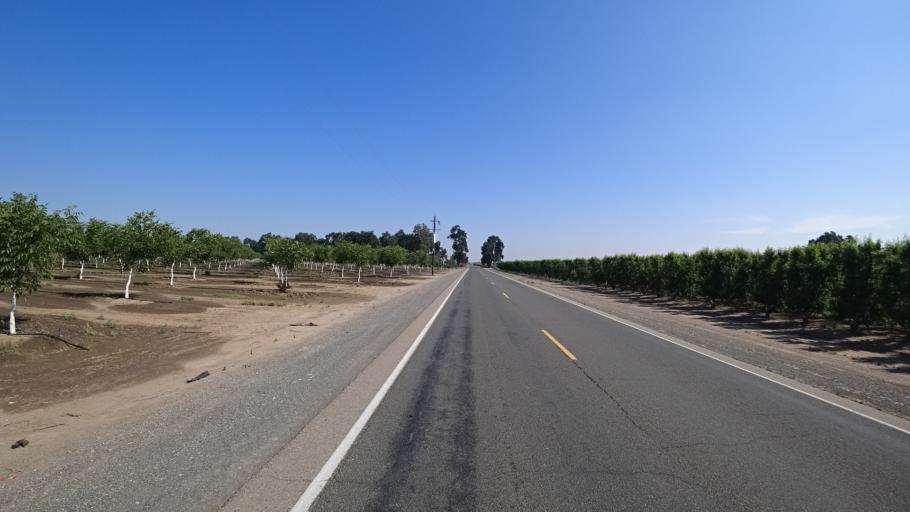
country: US
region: California
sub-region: Fresno County
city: Kingsburg
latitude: 36.4385
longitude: -119.5648
